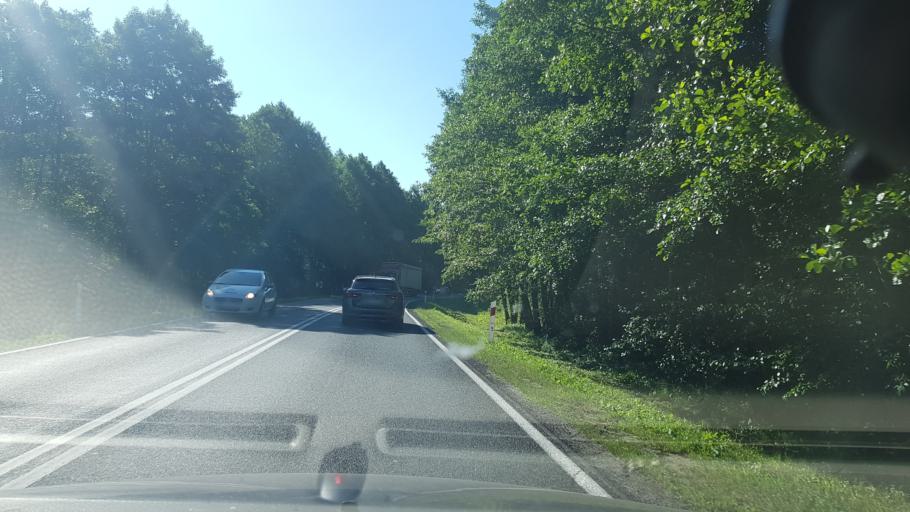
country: PL
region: Masovian Voivodeship
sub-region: Powiat wyszkowski
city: Branszczyk
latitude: 52.5804
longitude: 21.5327
